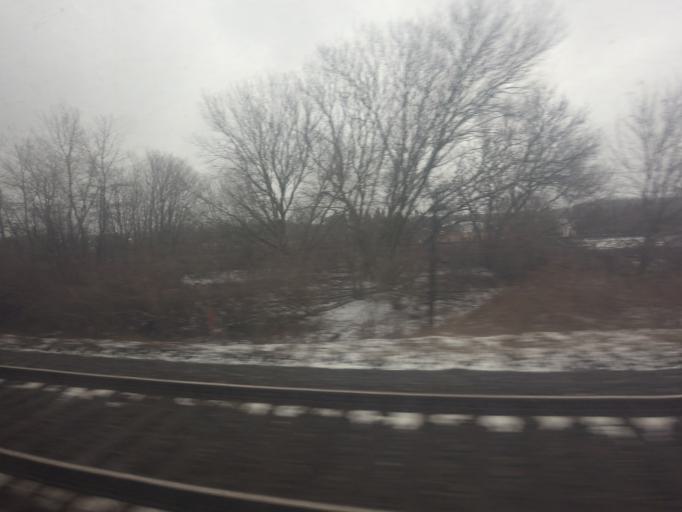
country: CA
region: Ontario
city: Quinte West
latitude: 44.0562
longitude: -77.6836
